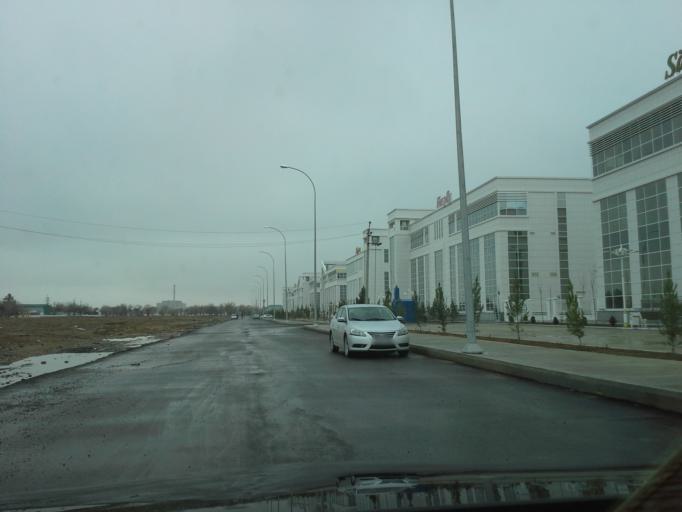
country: TM
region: Ahal
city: Ashgabat
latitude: 37.9507
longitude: 58.4307
